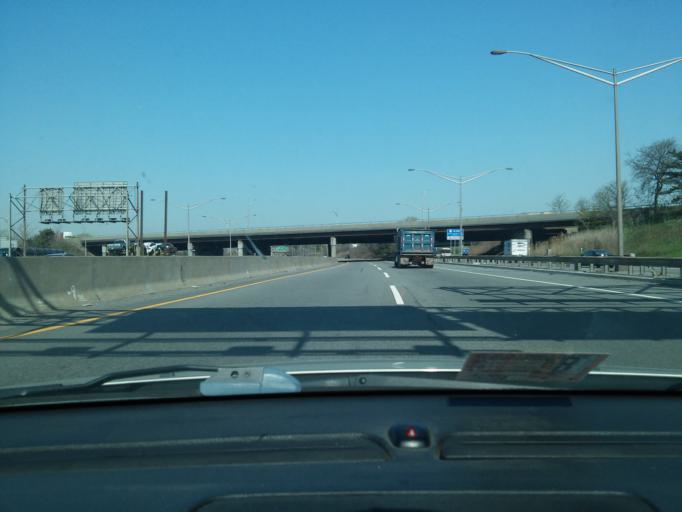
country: US
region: New Jersey
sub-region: Essex County
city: Newark
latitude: 40.7092
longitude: -74.1588
